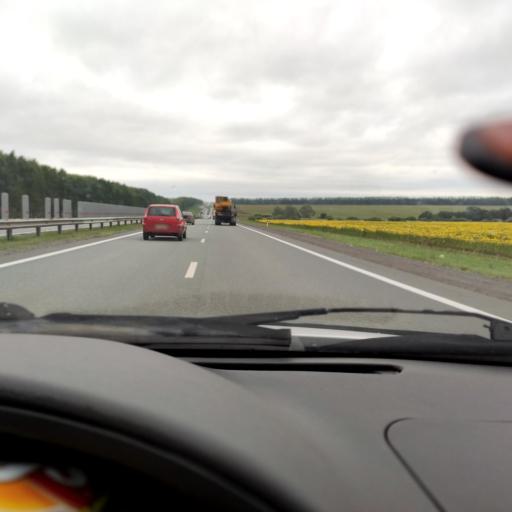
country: RU
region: Bashkortostan
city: Dmitriyevka
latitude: 54.7020
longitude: 55.2507
